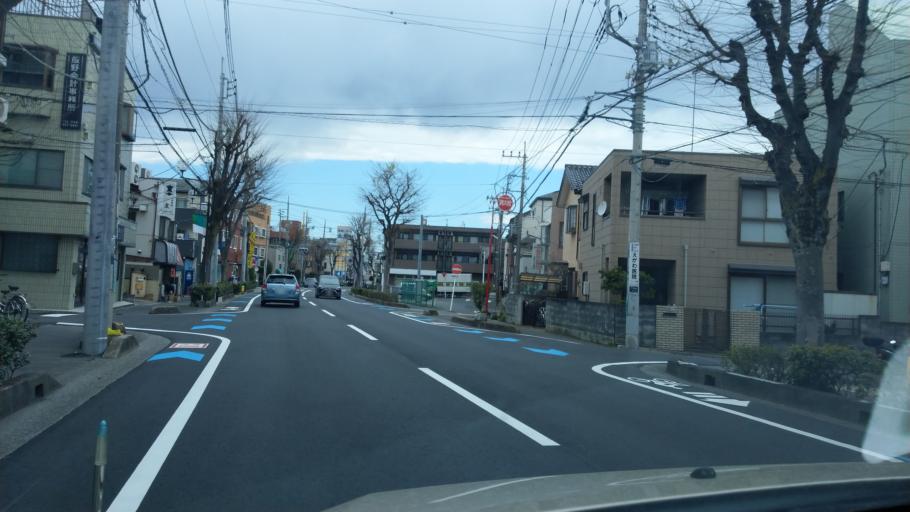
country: JP
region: Saitama
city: Yono
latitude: 35.8807
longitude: 139.6285
